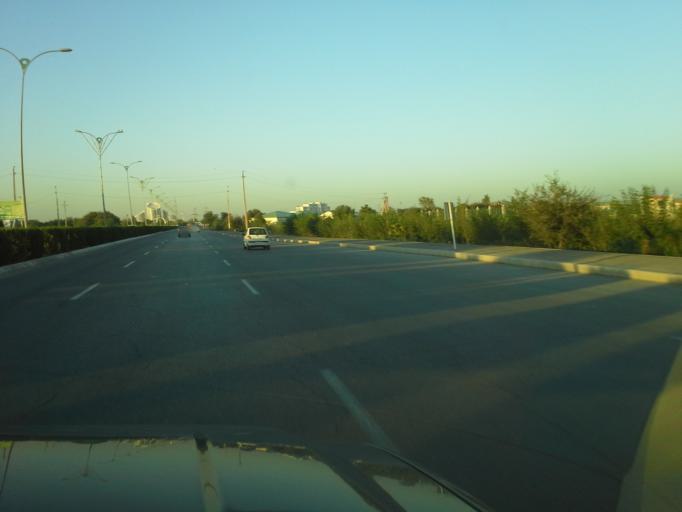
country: TM
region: Dasoguz
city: Dasoguz
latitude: 41.8165
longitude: 59.9176
